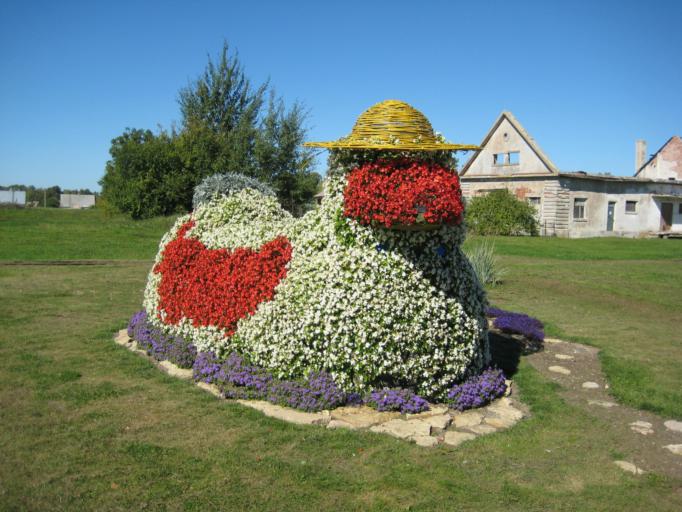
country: LT
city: Linkuva
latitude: 56.0826
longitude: 23.9667
